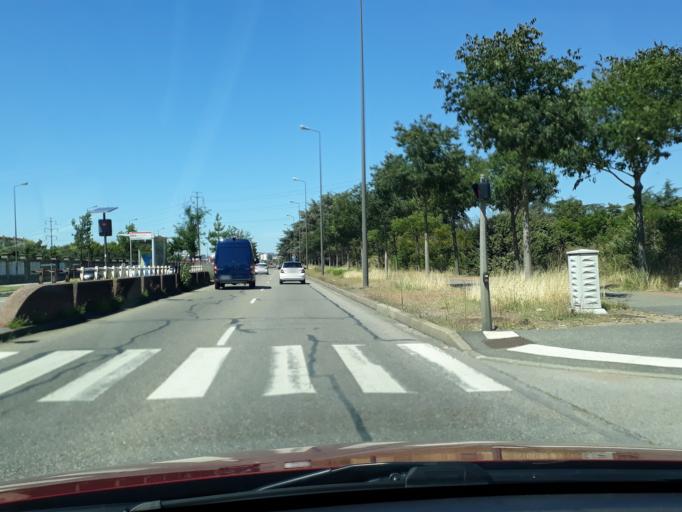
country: FR
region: Rhone-Alpes
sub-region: Departement du Rhone
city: Bron
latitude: 45.7131
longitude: 4.8990
